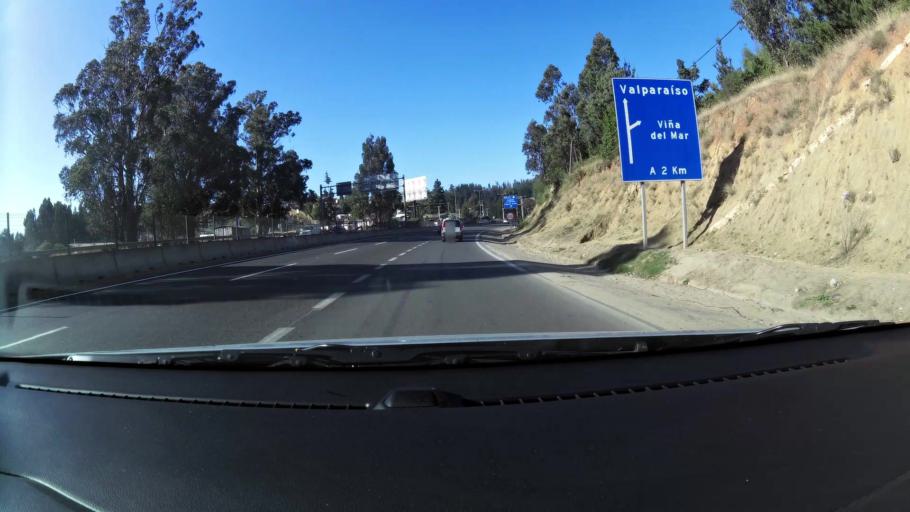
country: CL
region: Valparaiso
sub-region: Provincia de Valparaiso
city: Vina del Mar
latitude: -33.1120
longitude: -71.5599
